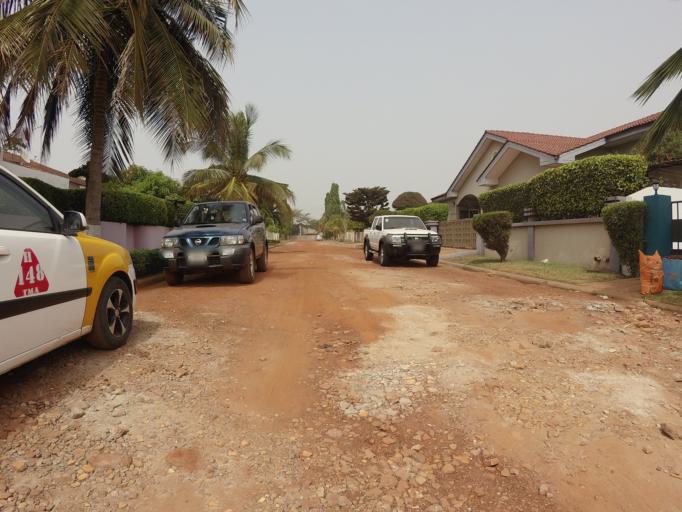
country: GH
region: Greater Accra
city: Teshi Old Town
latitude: 5.6210
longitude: -0.1256
